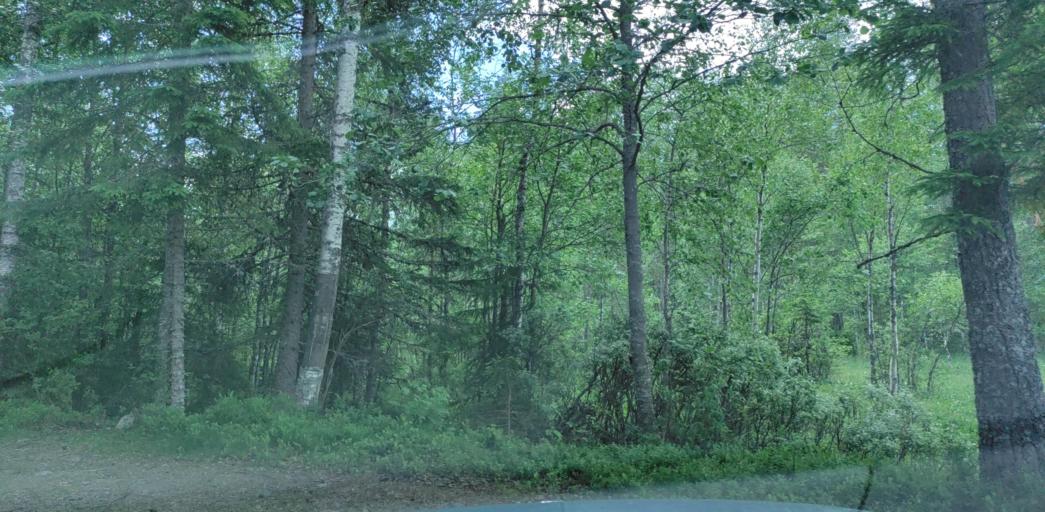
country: SE
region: Vaermland
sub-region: Hagfors Kommun
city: Ekshaerad
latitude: 60.0905
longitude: 13.3125
